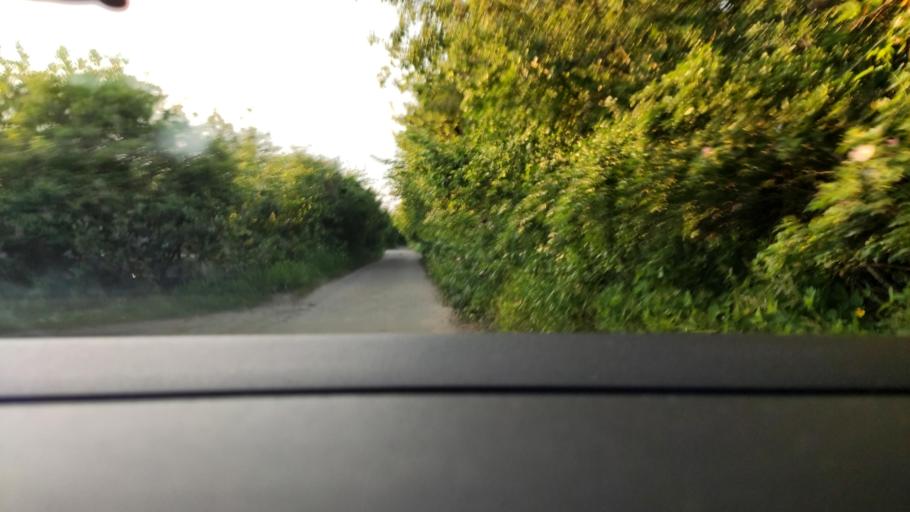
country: RU
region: Voronezj
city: Ramon'
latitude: 51.9087
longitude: 39.1770
